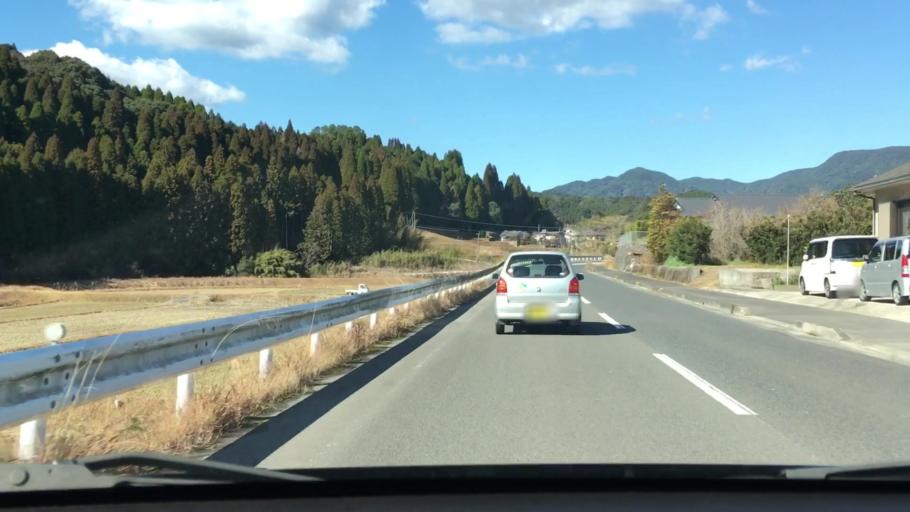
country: JP
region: Kagoshima
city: Ijuin
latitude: 31.6929
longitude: 130.4628
